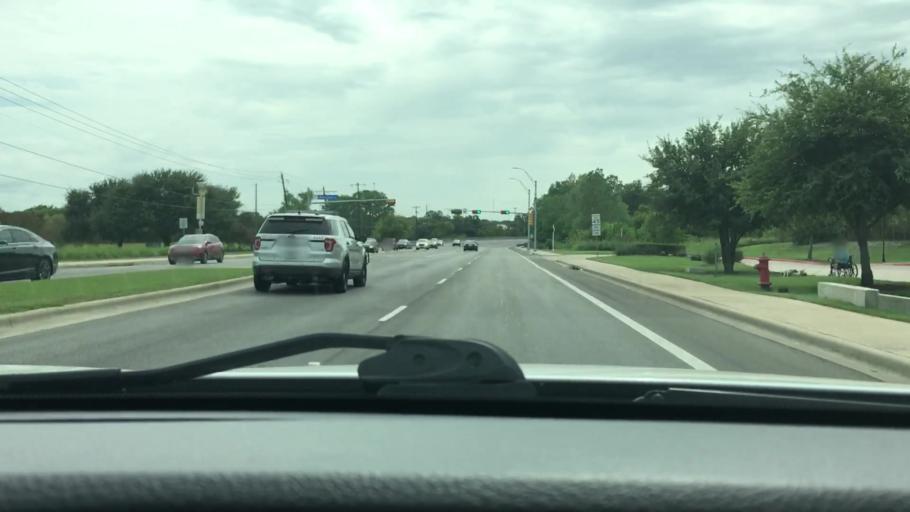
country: US
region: Texas
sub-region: Travis County
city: Windemere
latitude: 30.4642
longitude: -97.6459
